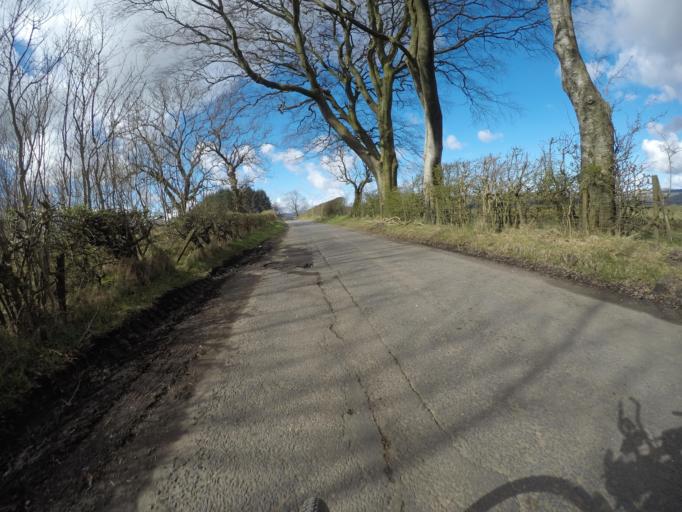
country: GB
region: Scotland
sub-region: North Ayrshire
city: Kilbirnie
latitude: 55.7211
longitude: -4.6681
